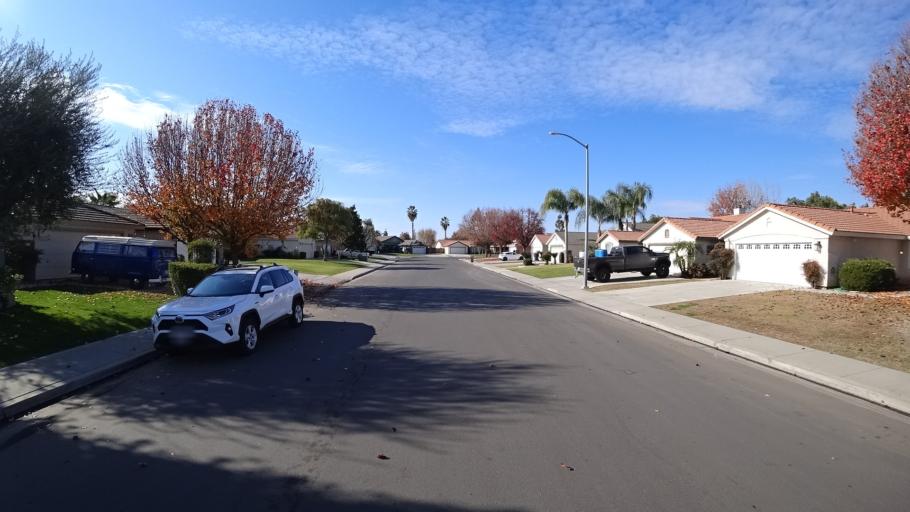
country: US
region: California
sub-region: Kern County
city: Greenacres
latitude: 35.4119
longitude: -119.0994
